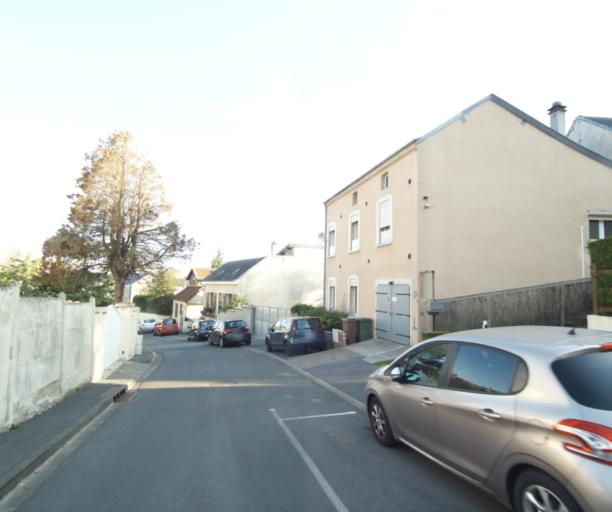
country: FR
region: Champagne-Ardenne
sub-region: Departement des Ardennes
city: Charleville-Mezieres
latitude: 49.7836
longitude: 4.7145
